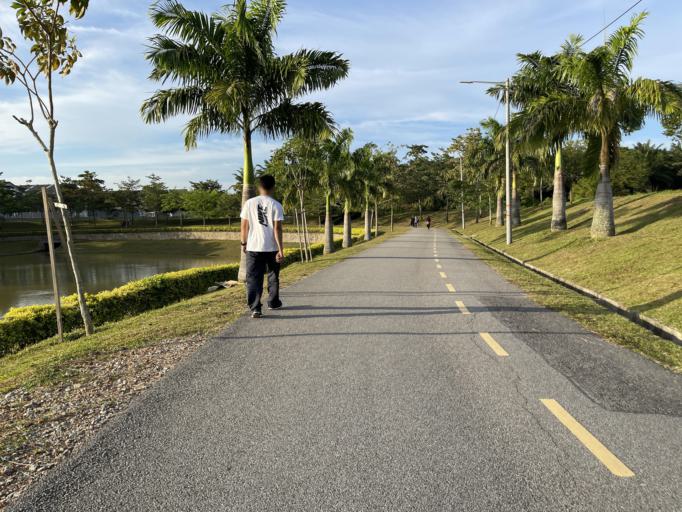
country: MY
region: Melaka
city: Kampung Ayer Keroh
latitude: 2.3152
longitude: 102.2448
